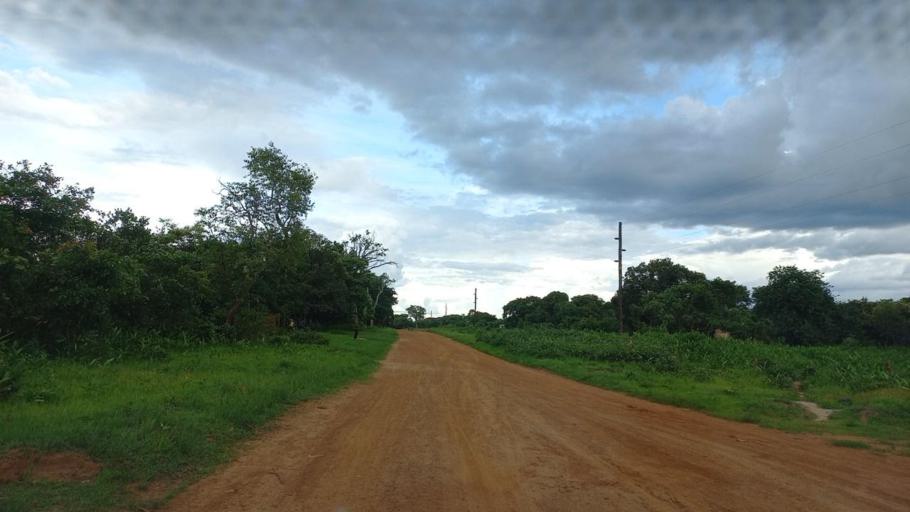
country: ZM
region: North-Western
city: Mwinilunga
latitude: -11.7739
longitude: 24.4000
